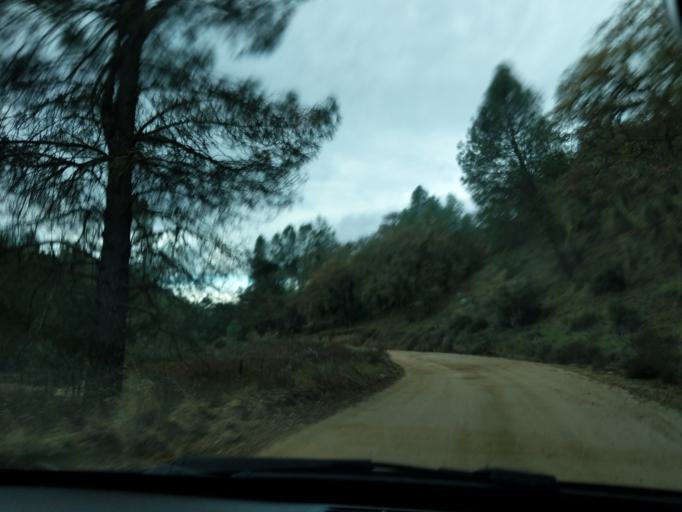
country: US
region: California
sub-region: Monterey County
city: Soledad
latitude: 36.5572
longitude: -121.2396
